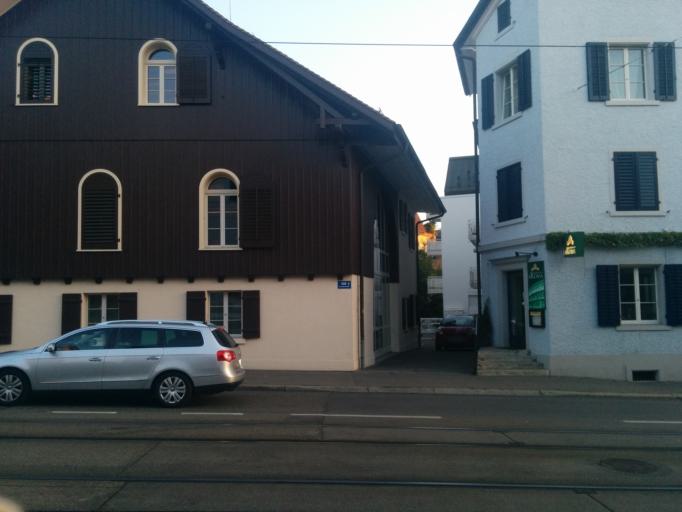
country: CH
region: Zurich
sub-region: Bezirk Zuerich
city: Zuerich (Kreis 7) / Hottingen
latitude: 47.3656
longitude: 8.5639
